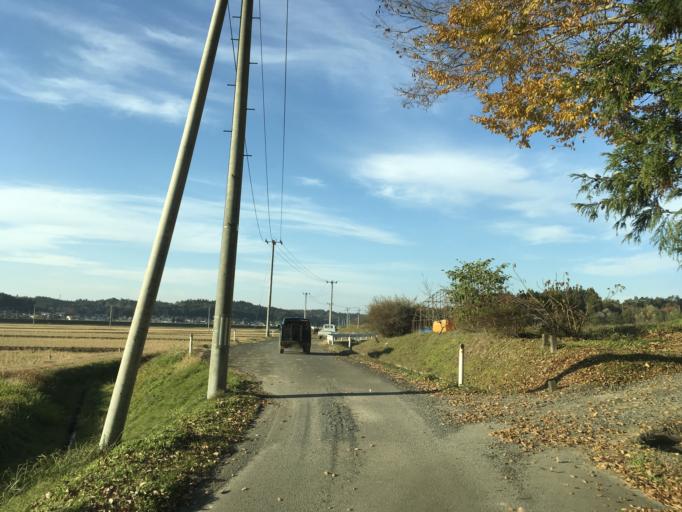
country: JP
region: Iwate
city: Ichinoseki
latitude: 38.7937
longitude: 141.1853
